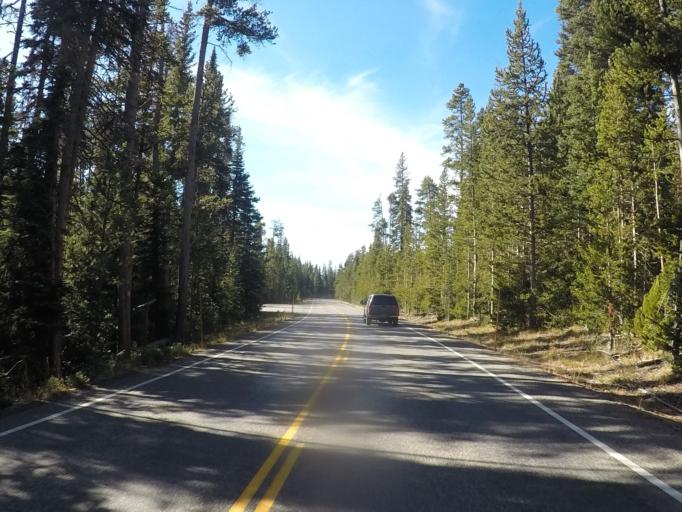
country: US
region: Montana
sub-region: Gallatin County
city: West Yellowstone
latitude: 44.4656
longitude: -110.4734
